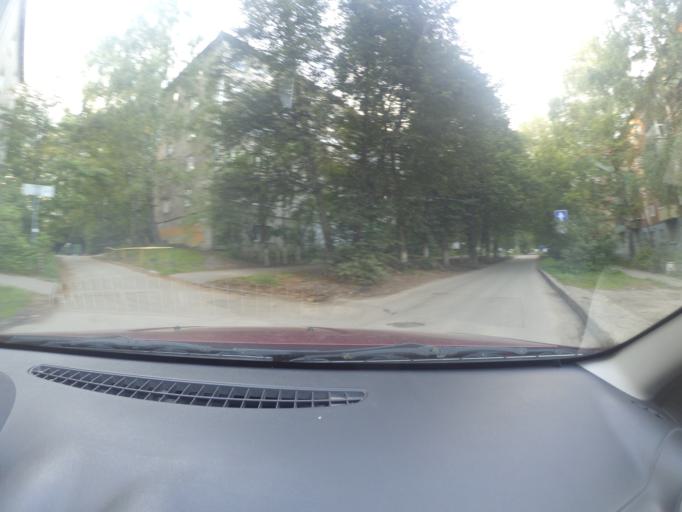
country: RU
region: Nizjnij Novgorod
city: Nizhniy Novgorod
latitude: 56.2795
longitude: 43.9867
